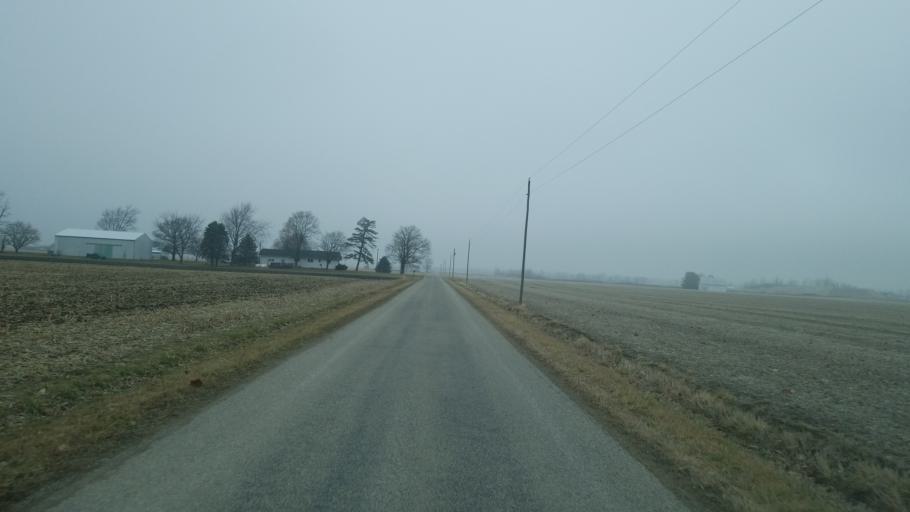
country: US
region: Indiana
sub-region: Adams County
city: Berne
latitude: 40.6493
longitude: -85.0608
